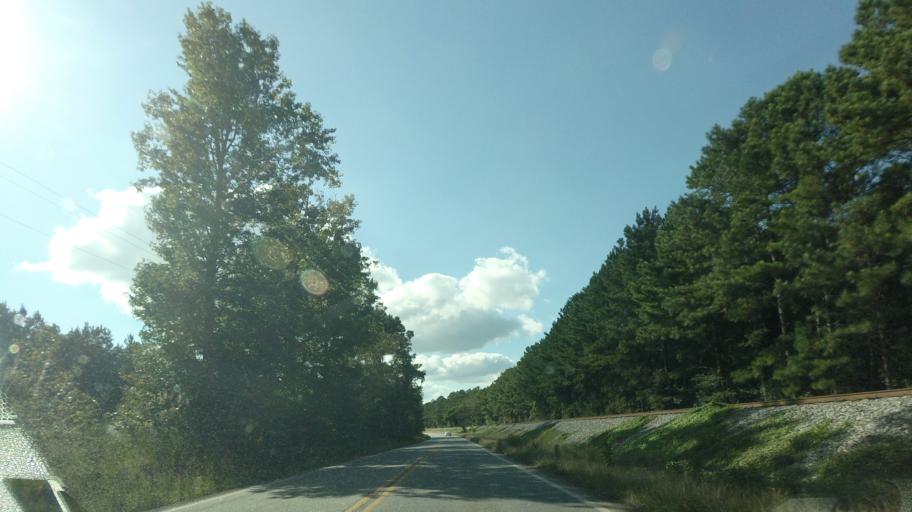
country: US
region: Georgia
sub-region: Monroe County
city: Forsyth
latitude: 33.0503
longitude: -84.0300
